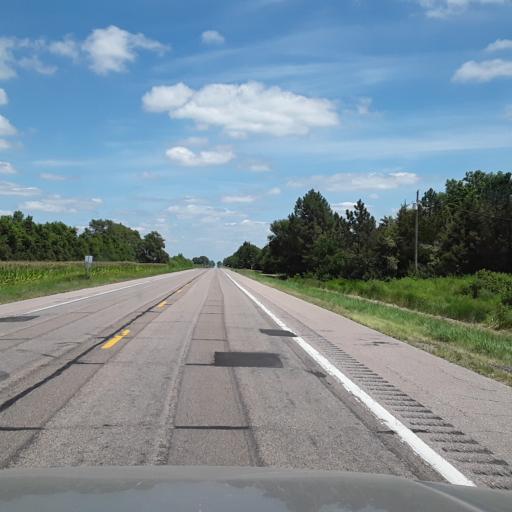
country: US
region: Nebraska
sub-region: Polk County
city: Osceola
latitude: 41.3610
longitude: -97.5573
